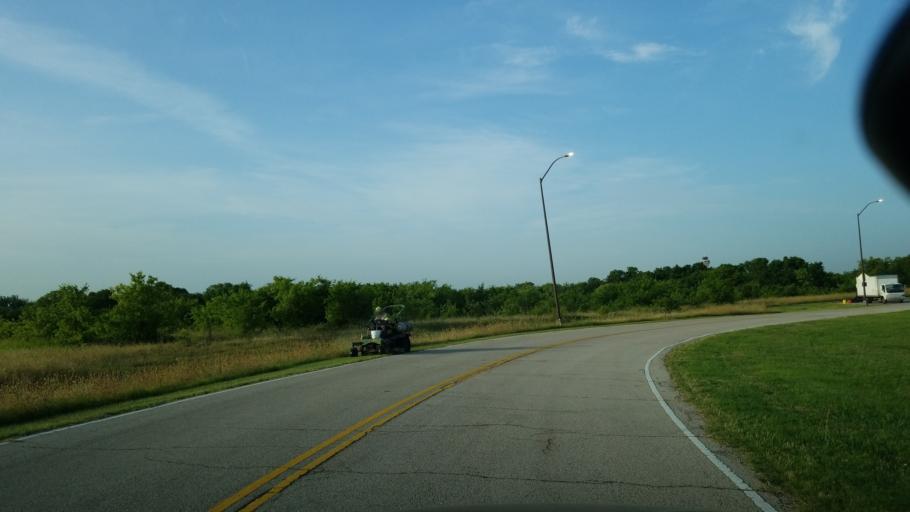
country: US
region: Texas
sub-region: Dallas County
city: Coppell
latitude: 32.9124
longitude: -97.0147
